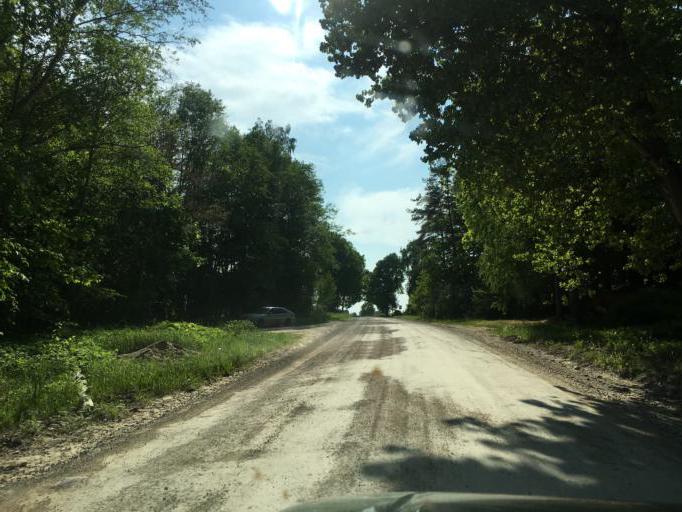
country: LV
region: Dundaga
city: Dundaga
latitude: 57.6072
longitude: 22.4678
